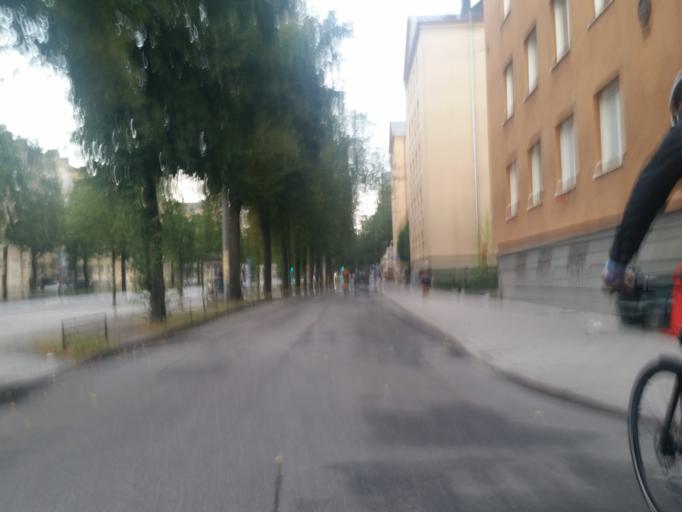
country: SE
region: Stockholm
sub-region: Stockholms Kommun
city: Arsta
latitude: 59.3078
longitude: 18.0697
